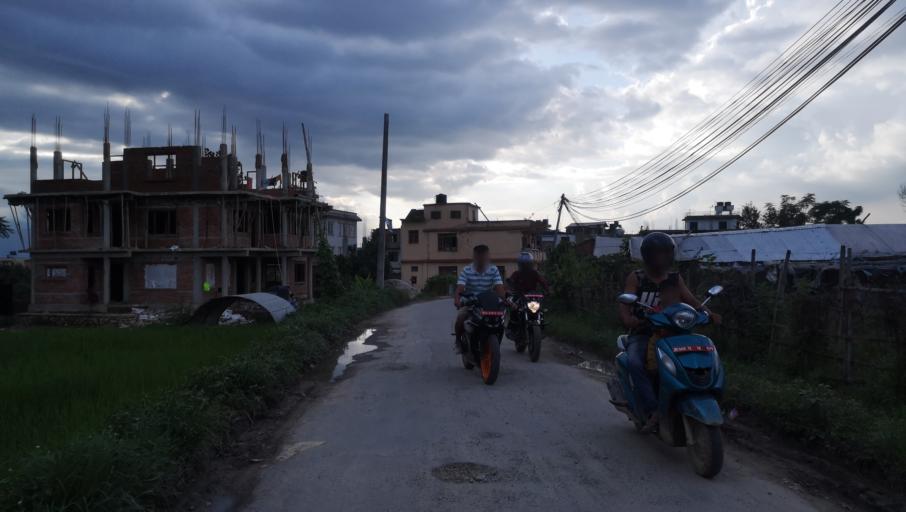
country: NP
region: Central Region
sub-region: Bagmati Zone
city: Bhaktapur
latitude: 27.6481
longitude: 85.3873
